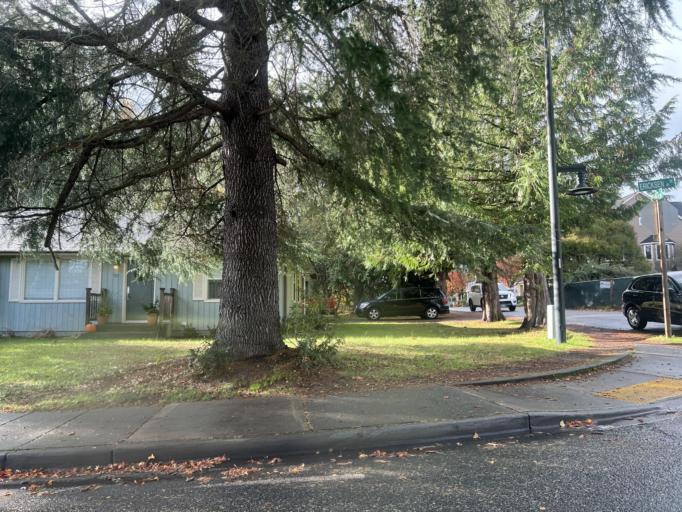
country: US
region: Washington
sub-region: Kitsap County
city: Bainbridge Island
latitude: 47.6284
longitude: -122.5170
